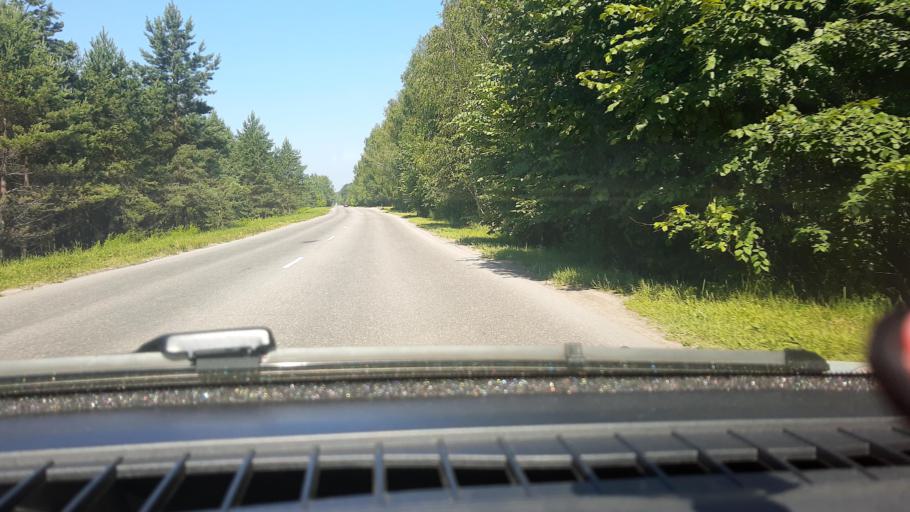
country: RU
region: Nizjnij Novgorod
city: Afonino
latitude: 56.3151
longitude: 44.1635
